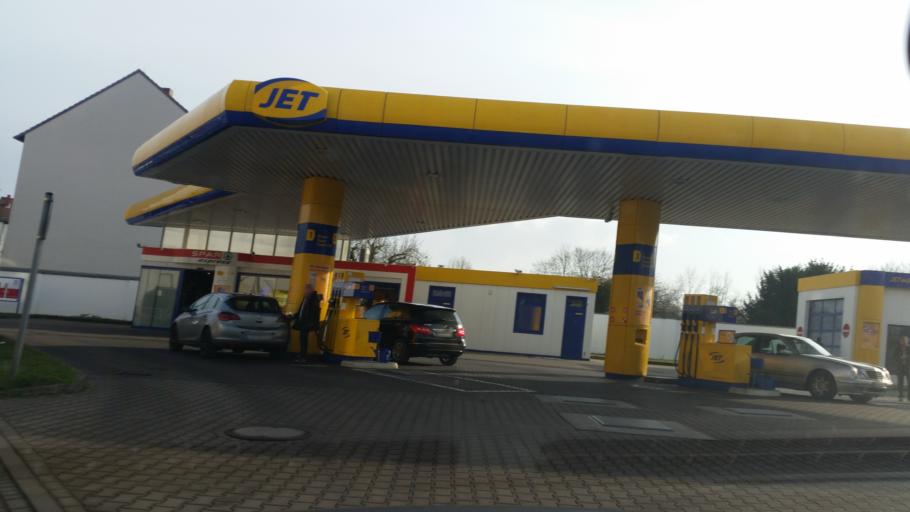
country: DE
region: Lower Saxony
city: Hameln
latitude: 52.0983
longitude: 9.3622
